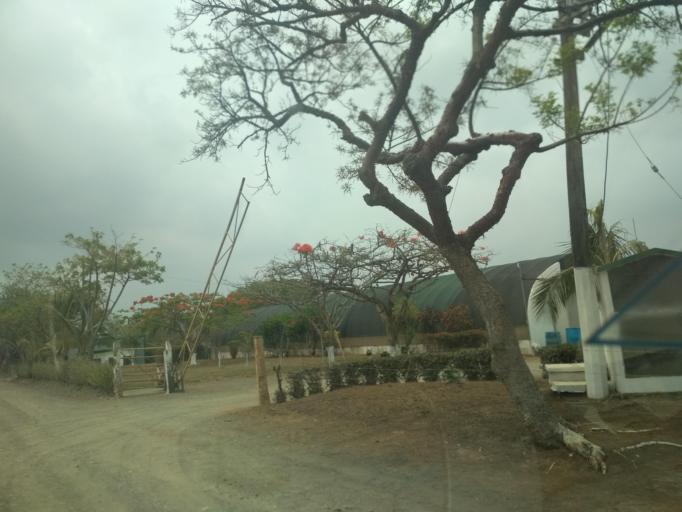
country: MX
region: Veracruz
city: Paso del Toro
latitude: 19.0076
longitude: -96.1327
